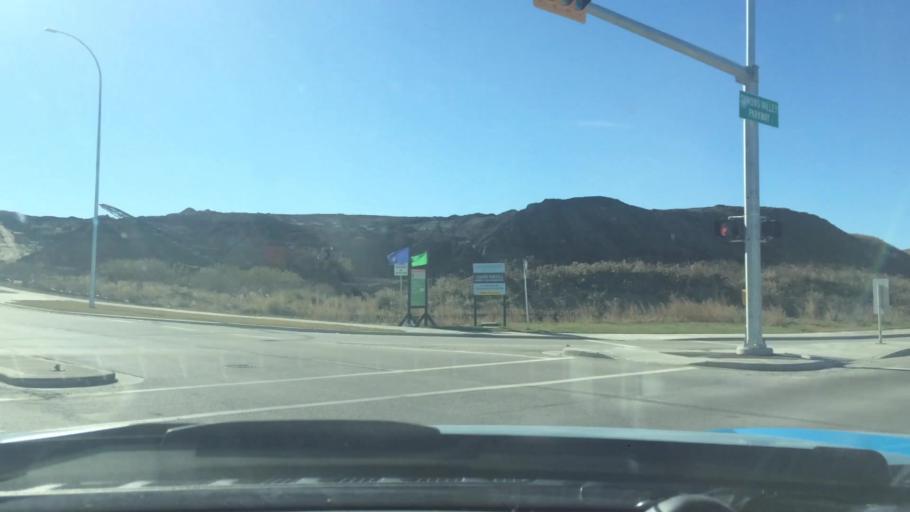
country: CA
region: Alberta
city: Calgary
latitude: 51.1680
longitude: -114.1606
